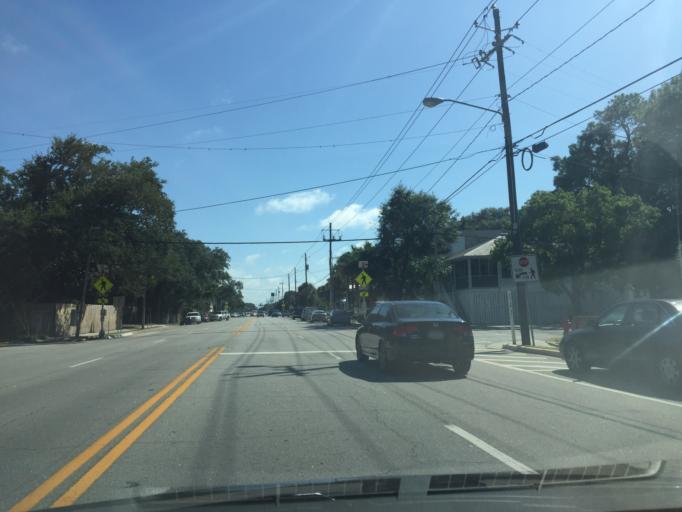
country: US
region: Georgia
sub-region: Chatham County
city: Tybee Island
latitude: 31.9985
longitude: -80.8469
